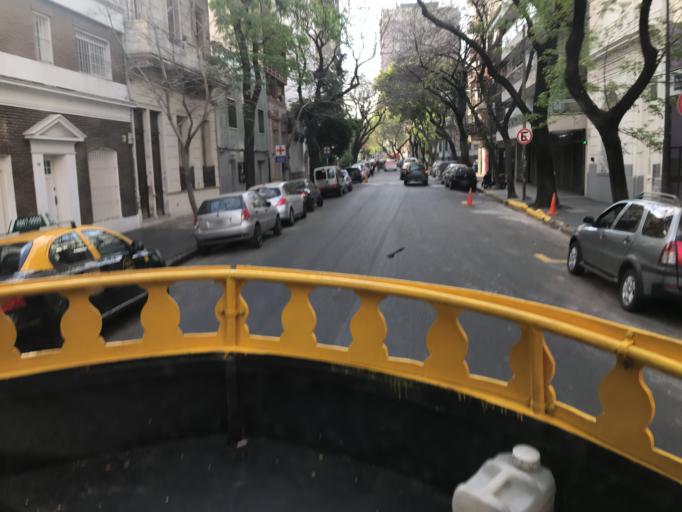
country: AR
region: Buenos Aires F.D.
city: Retiro
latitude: -34.5926
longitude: -58.4161
